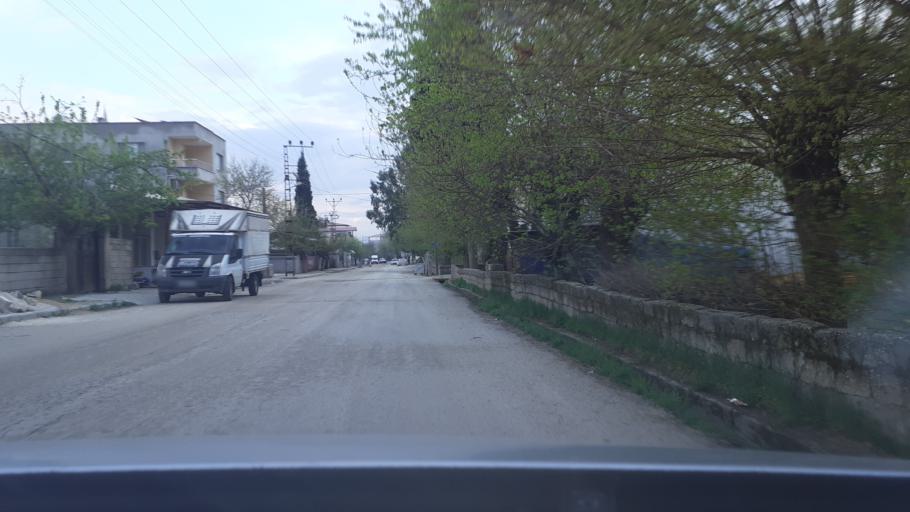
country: TR
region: Hatay
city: Kirikhan
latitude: 36.4852
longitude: 36.3502
